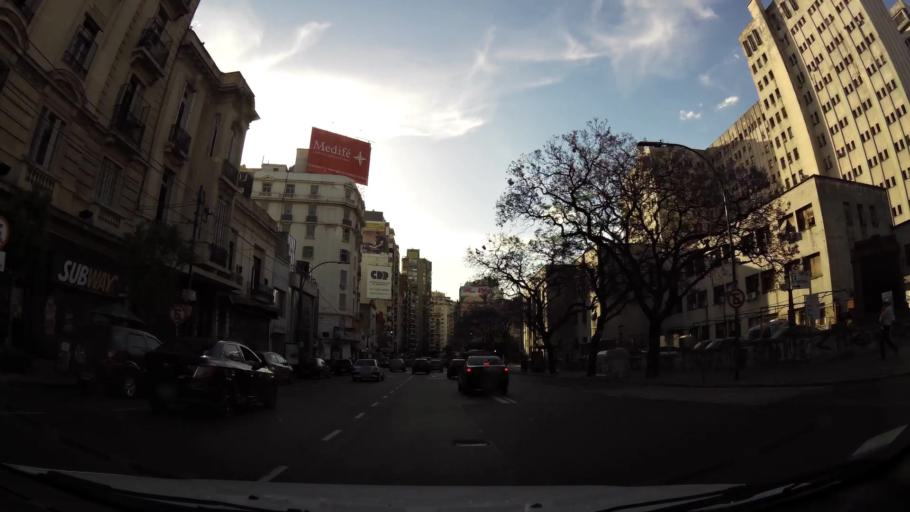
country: AR
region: Buenos Aires F.D.
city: Retiro
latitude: -34.5996
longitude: -58.3994
